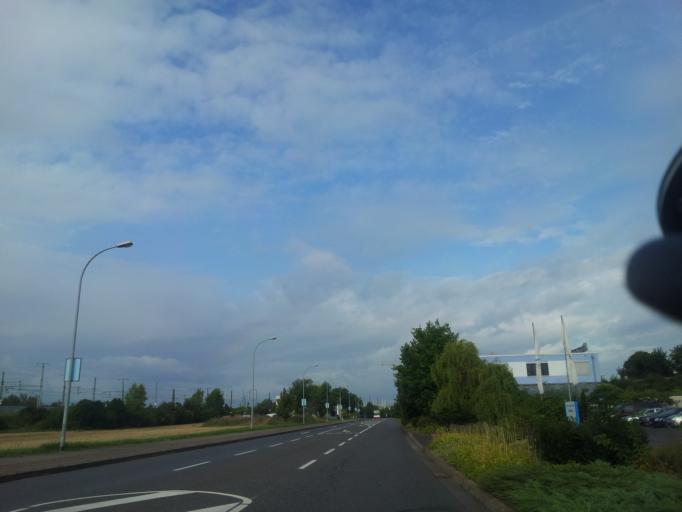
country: DE
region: Saxony-Anhalt
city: Peissen
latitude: 51.5011
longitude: 12.0295
